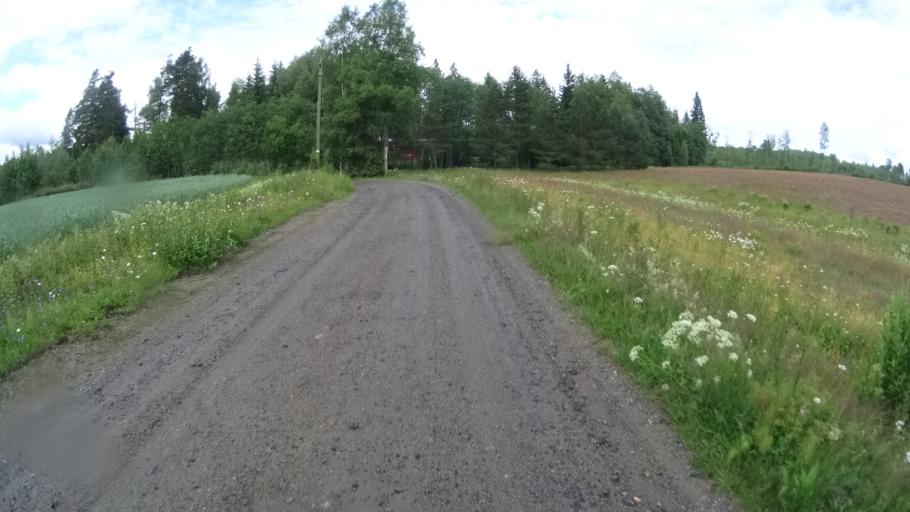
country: FI
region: Uusimaa
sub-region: Helsinki
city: Karkkila
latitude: 60.5874
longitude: 24.3396
